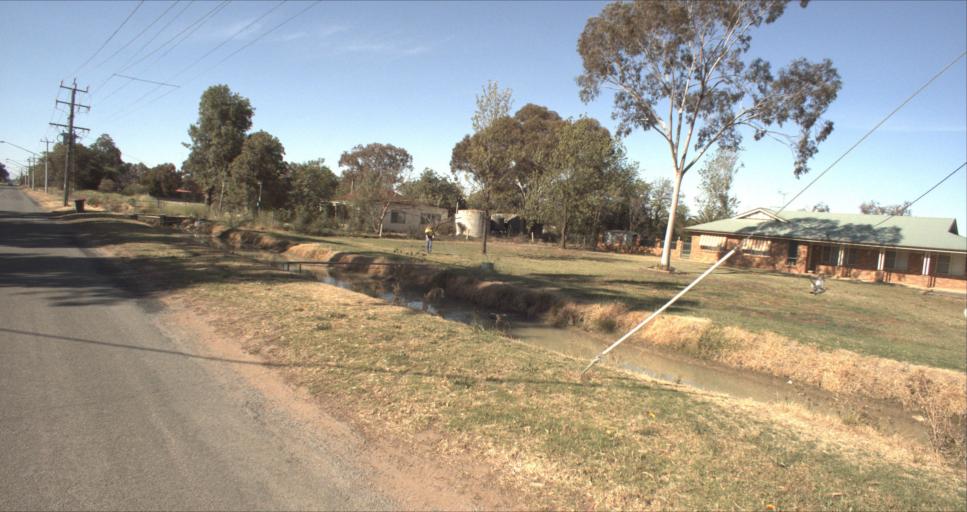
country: AU
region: New South Wales
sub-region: Leeton
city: Leeton
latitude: -34.5694
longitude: 146.4138
